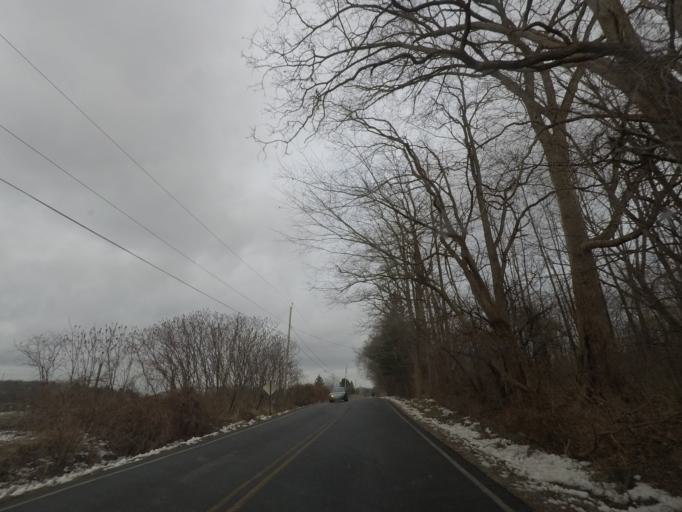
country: US
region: New York
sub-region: Rensselaer County
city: East Greenbush
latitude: 42.5844
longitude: -73.7184
